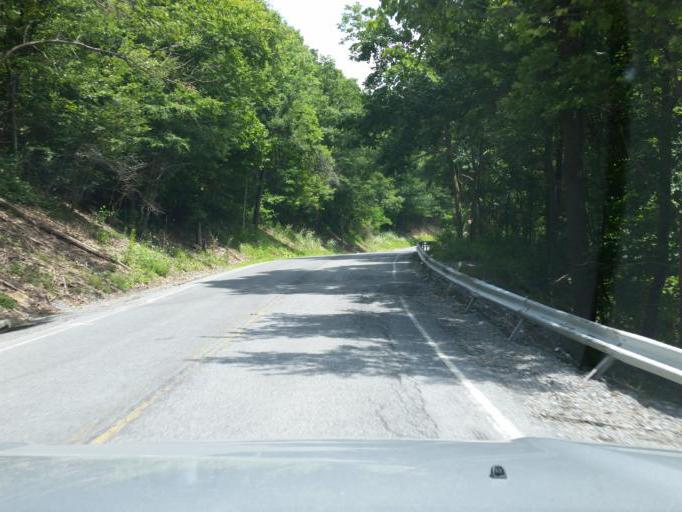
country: US
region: Pennsylvania
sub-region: Blair County
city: Altoona
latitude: 40.5561
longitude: -78.4520
